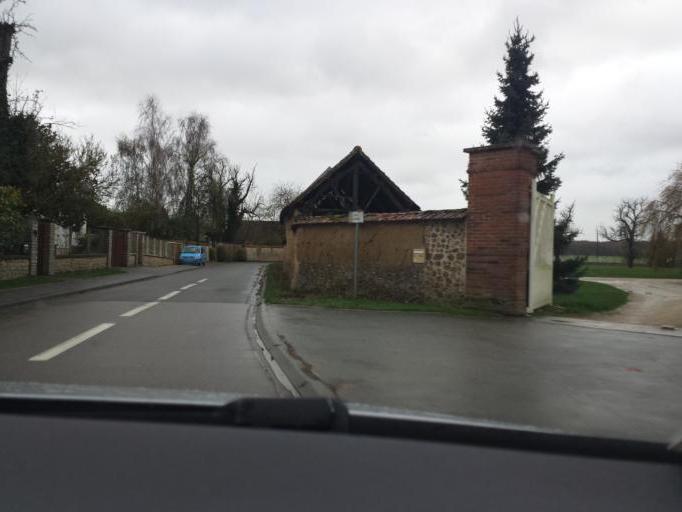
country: FR
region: Haute-Normandie
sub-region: Departement de l'Eure
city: Gravigny
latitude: 49.0060
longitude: 1.2198
